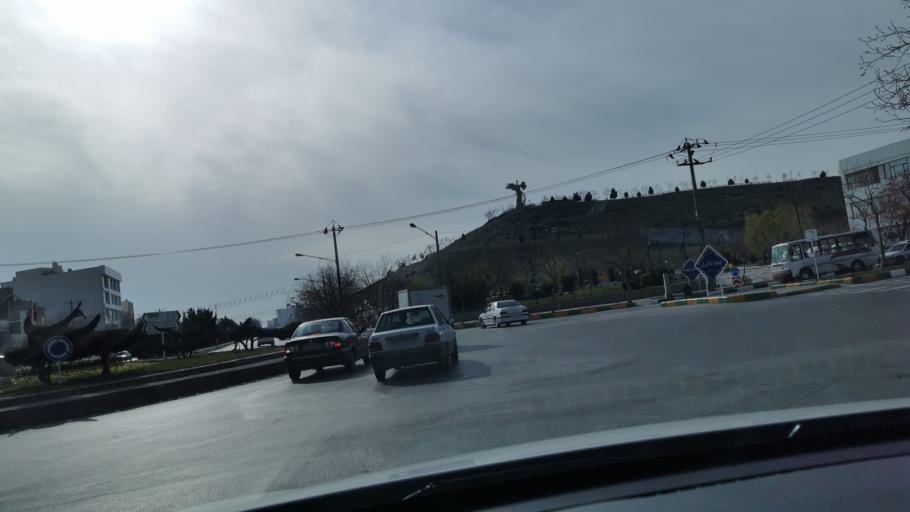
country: IR
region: Razavi Khorasan
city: Mashhad
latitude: 36.2961
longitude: 59.5290
